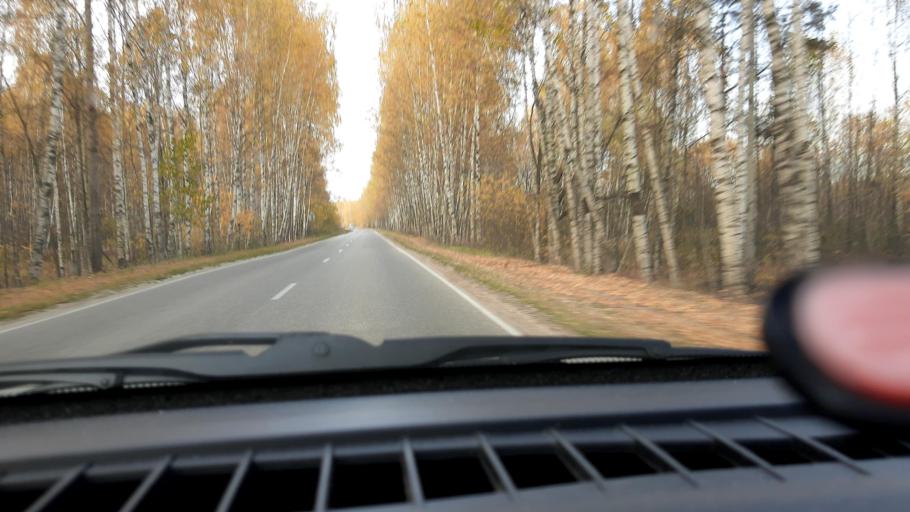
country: RU
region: Nizjnij Novgorod
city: Neklyudovo
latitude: 56.5182
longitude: 43.8373
